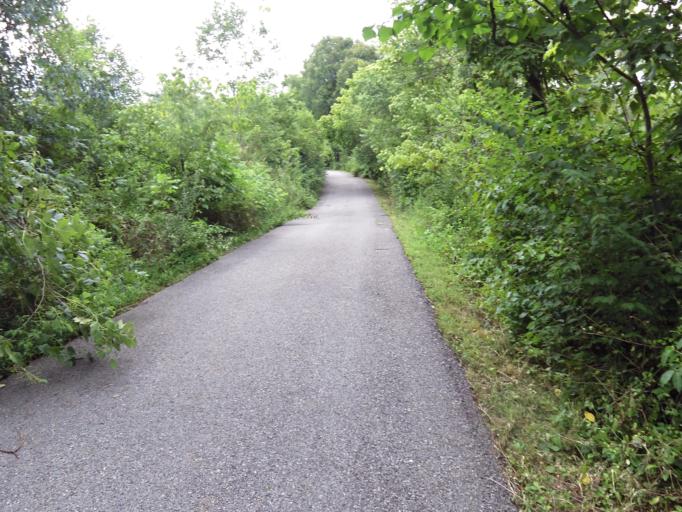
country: US
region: Tennessee
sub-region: Knox County
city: Farragut
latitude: 35.9032
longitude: -84.1454
